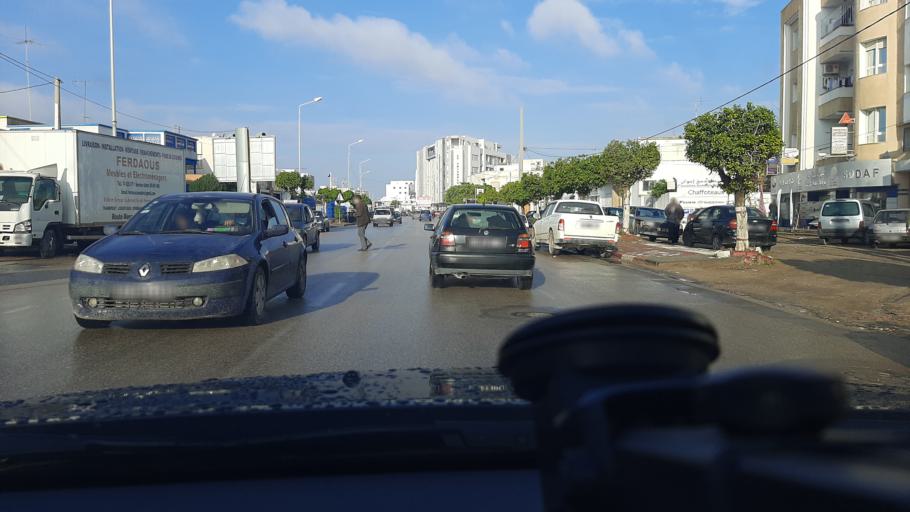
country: TN
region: Safaqis
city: Sfax
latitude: 34.7465
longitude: 10.7253
